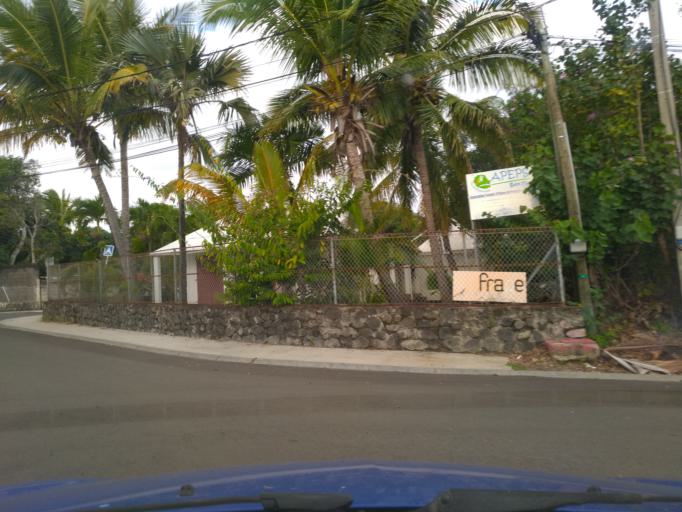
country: RE
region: Reunion
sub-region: Reunion
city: Saint-Pierre
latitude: -21.3300
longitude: 55.4757
